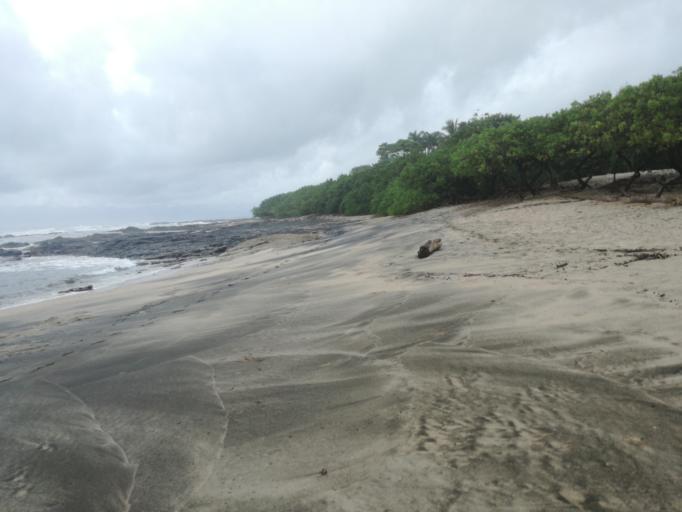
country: CR
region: Guanacaste
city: Santa Cruz
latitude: 10.2887
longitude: -85.8521
